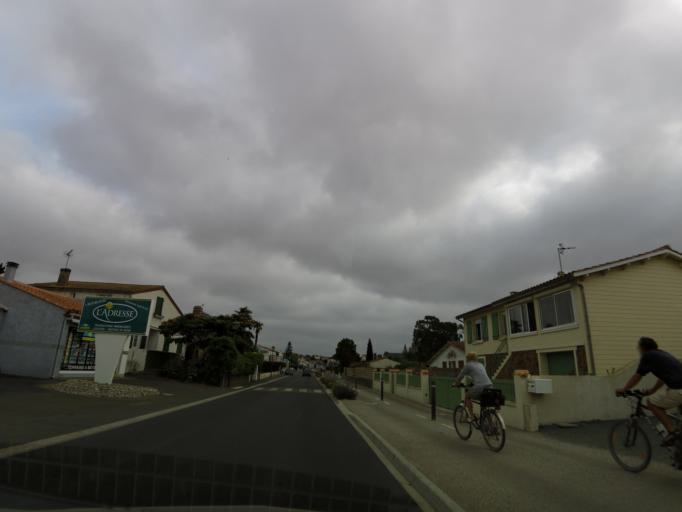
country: FR
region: Pays de la Loire
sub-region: Departement de la Vendee
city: Longeville-sur-Mer
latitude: 46.4207
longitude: -1.4935
